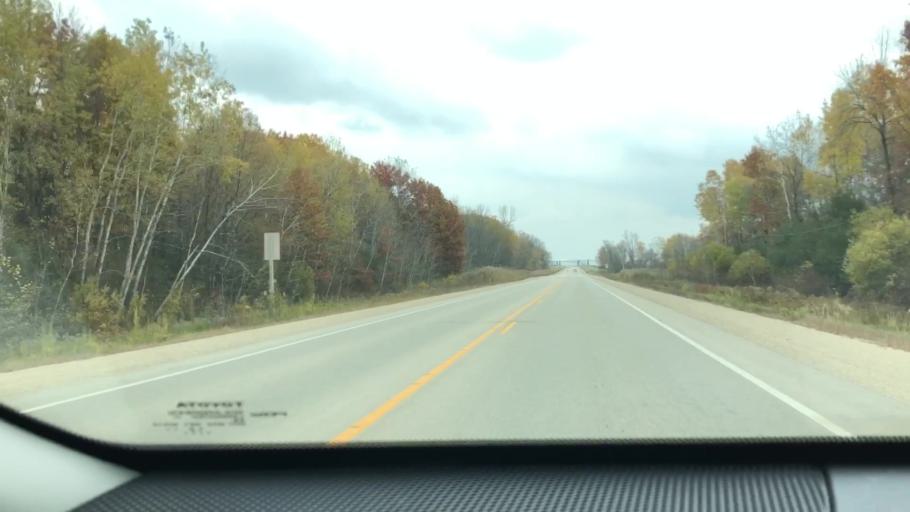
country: US
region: Wisconsin
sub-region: Brown County
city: Oneida
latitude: 44.4992
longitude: -88.1461
